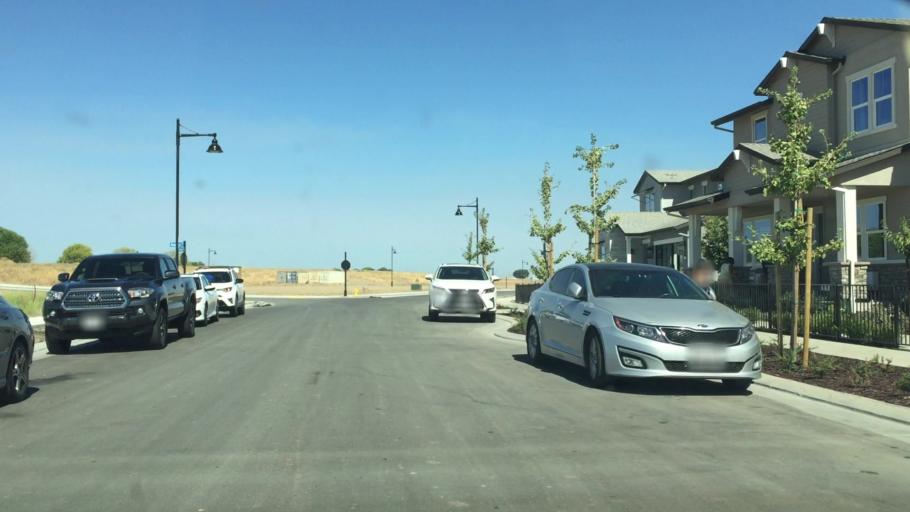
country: US
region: California
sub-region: San Joaquin County
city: Lathrop
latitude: 37.8040
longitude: -121.3270
